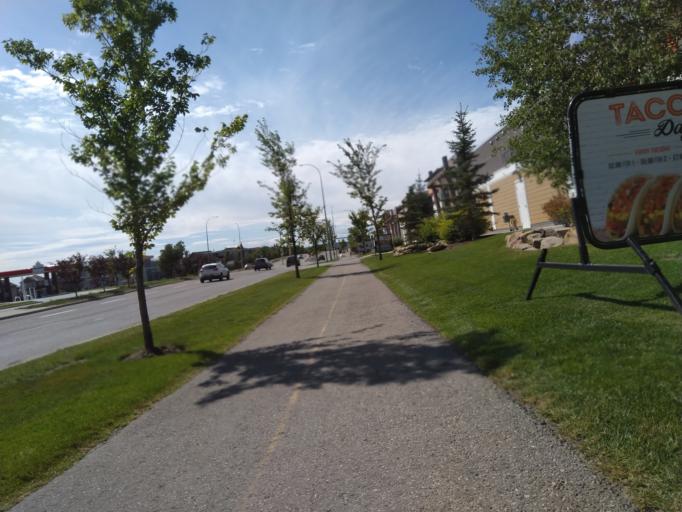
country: CA
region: Alberta
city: Calgary
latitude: 51.1748
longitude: -114.1080
